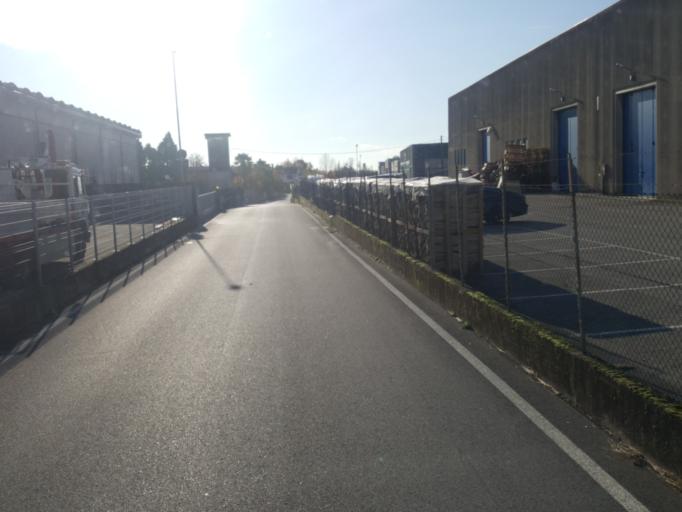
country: IT
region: Veneto
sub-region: Provincia di Treviso
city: One
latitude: 45.7842
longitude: 11.8875
